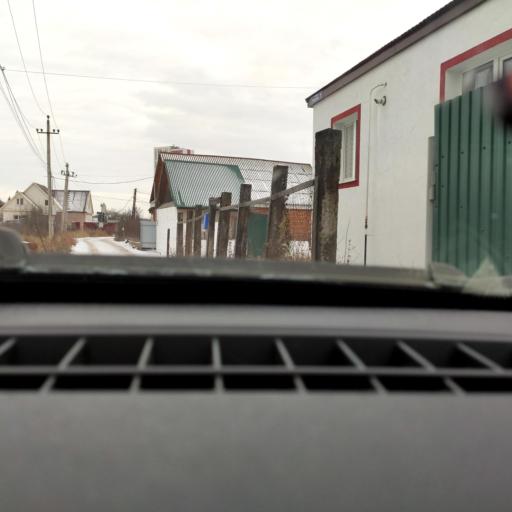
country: RU
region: Bashkortostan
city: Mikhaylovka
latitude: 54.7041
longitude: 55.8634
